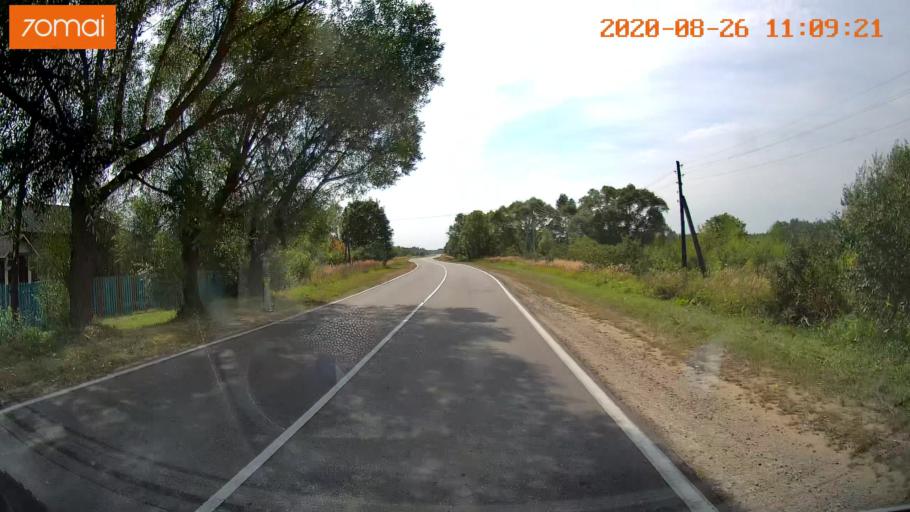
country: RU
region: Rjazan
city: Izhevskoye
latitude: 54.4921
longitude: 41.1236
